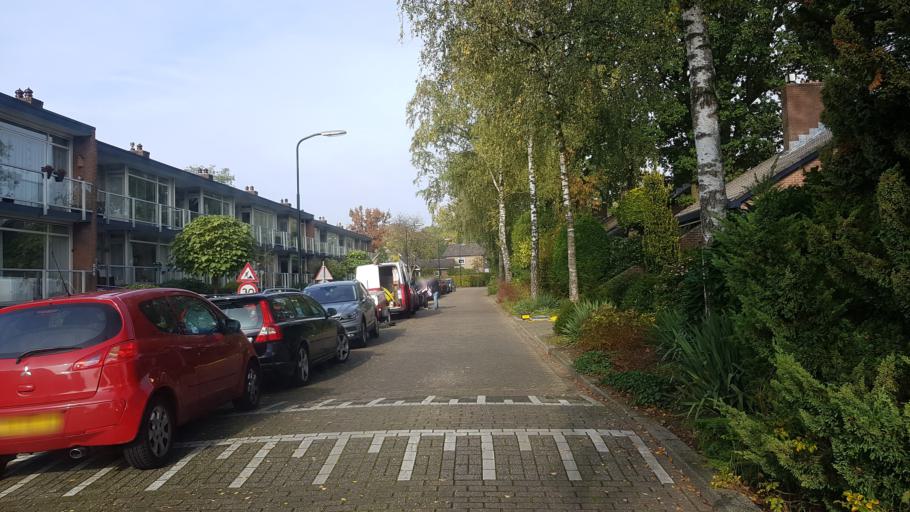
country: NL
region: Gelderland
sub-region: Gemeente Apeldoorn
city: Apeldoorn
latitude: 52.2060
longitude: 5.9328
